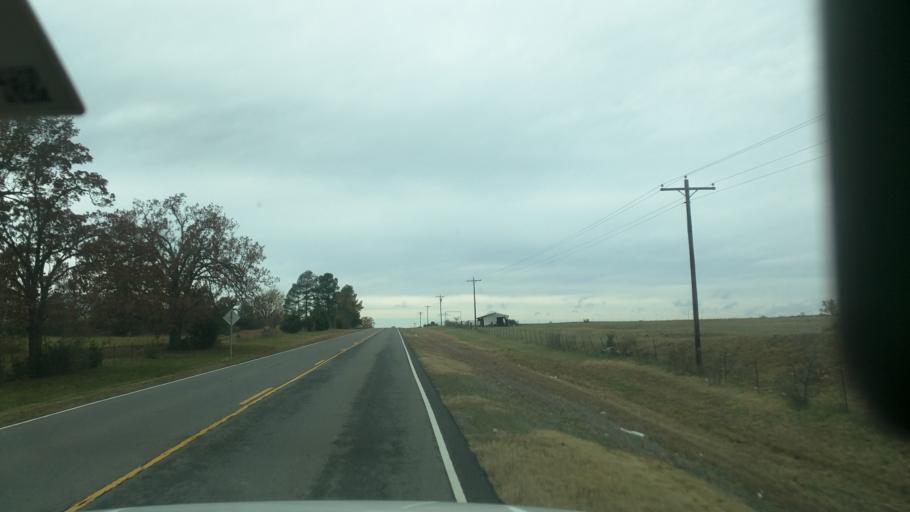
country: US
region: Oklahoma
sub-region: Cherokee County
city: Park Hill
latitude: 35.8963
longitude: -94.7859
